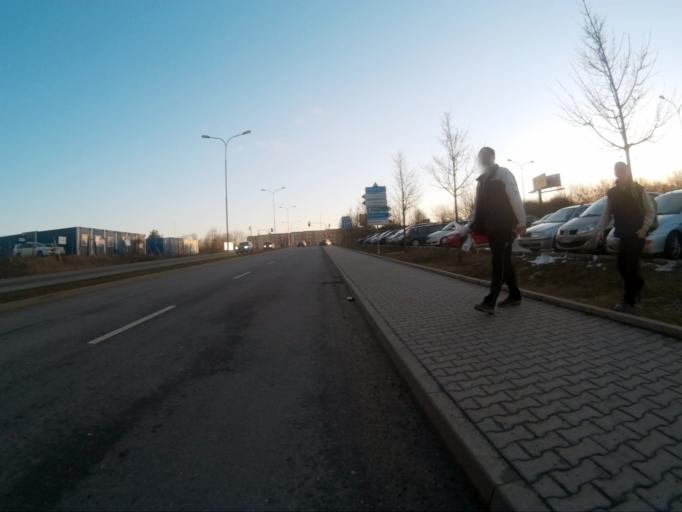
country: CZ
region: South Moravian
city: Ostopovice
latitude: 49.1752
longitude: 16.5643
